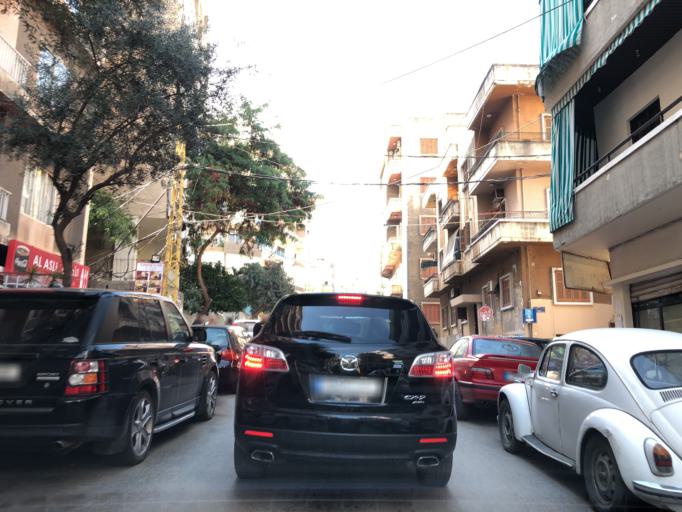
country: LB
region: Beyrouth
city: Beirut
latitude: 33.8873
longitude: 35.5298
